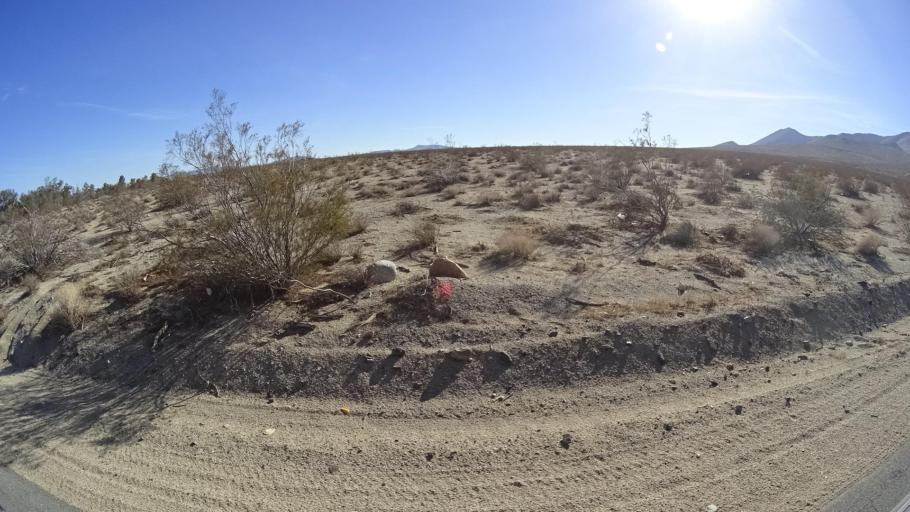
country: US
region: California
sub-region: Kern County
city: Inyokern
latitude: 35.6812
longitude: -117.8589
